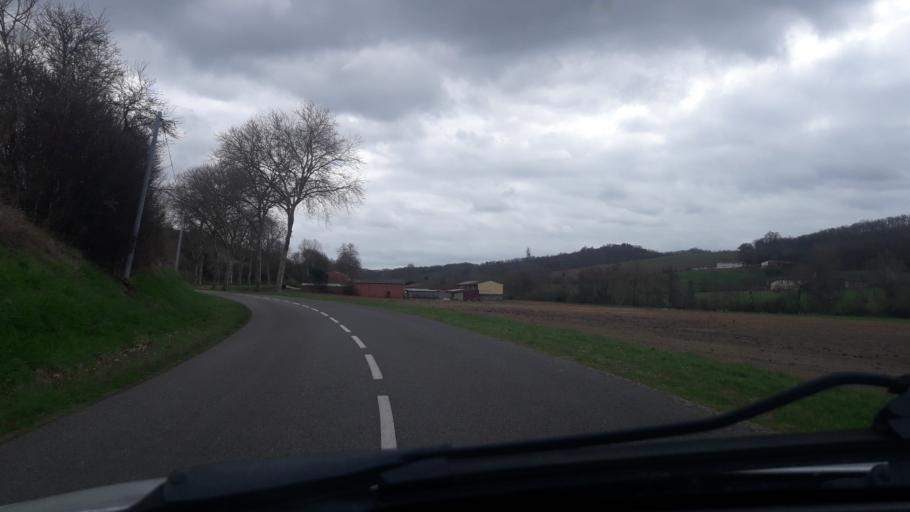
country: FR
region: Midi-Pyrenees
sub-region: Departement de la Haute-Garonne
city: Montesquieu-Volvestre
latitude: 43.2415
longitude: 1.2664
